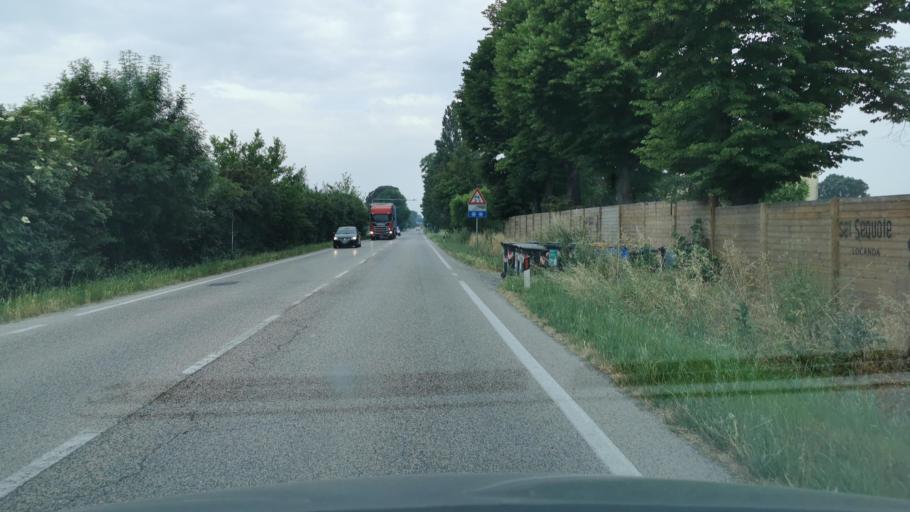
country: IT
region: Emilia-Romagna
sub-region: Provincia di Ravenna
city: Fornace Zarattini
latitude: 44.4113
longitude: 12.1240
